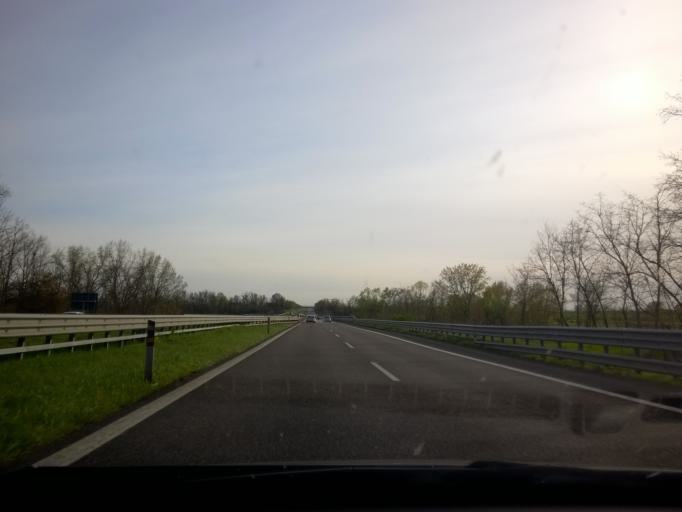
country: IT
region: Lombardy
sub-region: Provincia di Brescia
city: Manerbio
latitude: 45.3564
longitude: 10.1651
